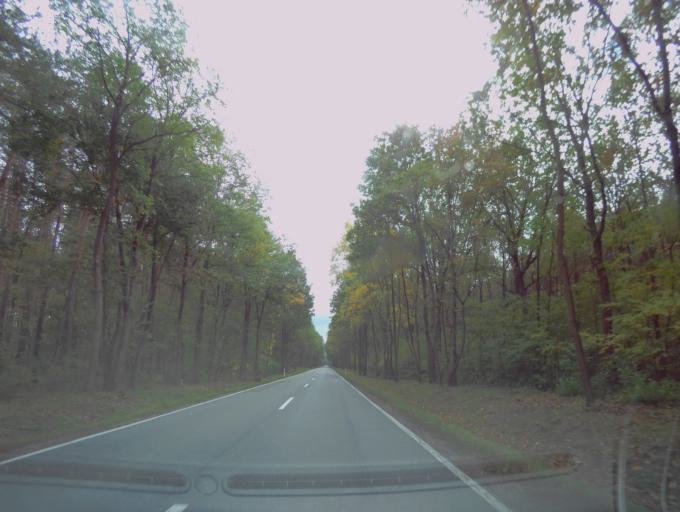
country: PL
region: Subcarpathian Voivodeship
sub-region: Powiat nizanski
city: Krzeszow
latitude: 50.3956
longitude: 22.2988
